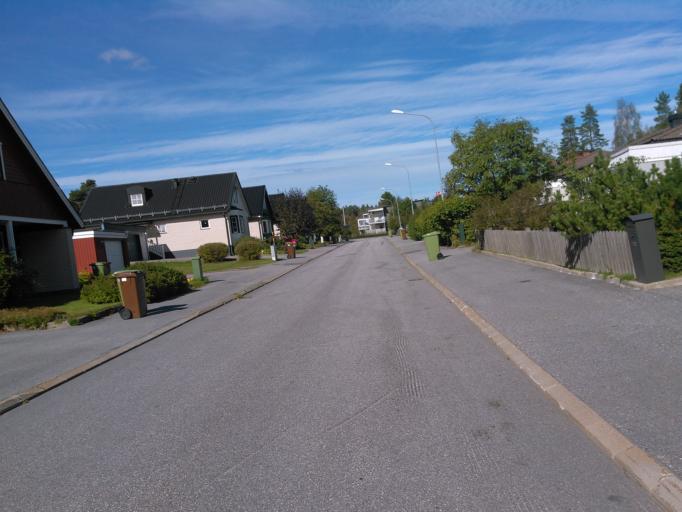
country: SE
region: Vaesterbotten
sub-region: Umea Kommun
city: Umea
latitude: 63.7970
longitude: 20.3131
